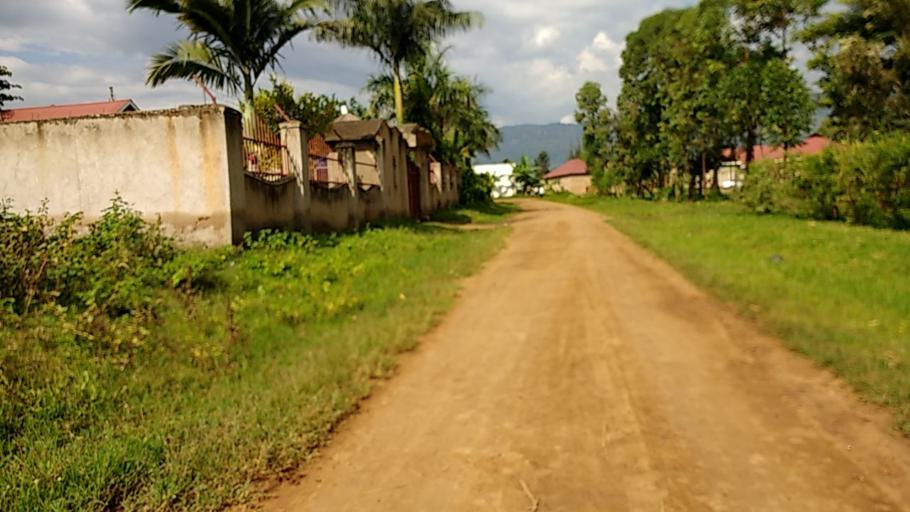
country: UG
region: Eastern Region
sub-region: Mbale District
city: Mbale
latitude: 1.0664
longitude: 34.1689
